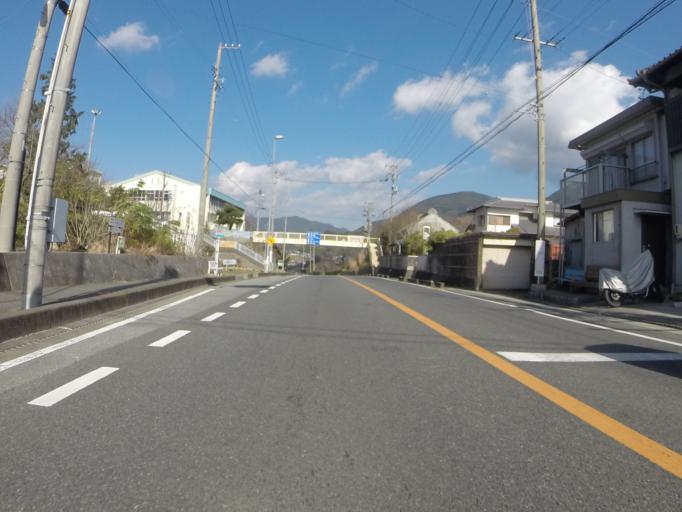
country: JP
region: Shizuoka
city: Fujinomiya
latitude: 35.0911
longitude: 138.5162
